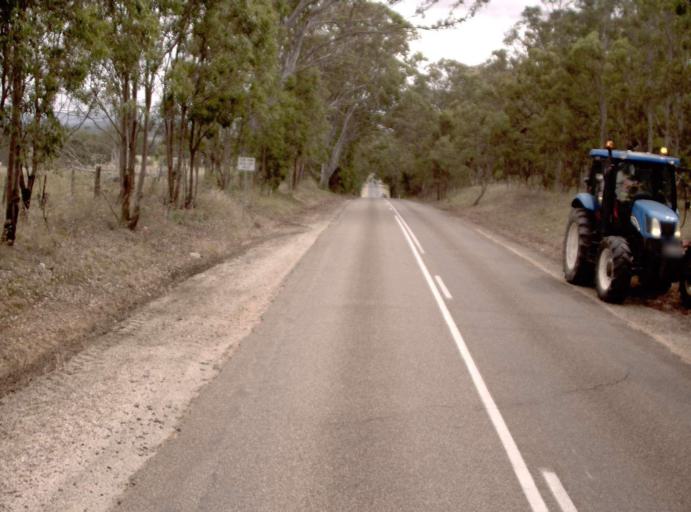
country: AU
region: Victoria
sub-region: Wellington
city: Sale
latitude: -37.8527
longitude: 147.0708
